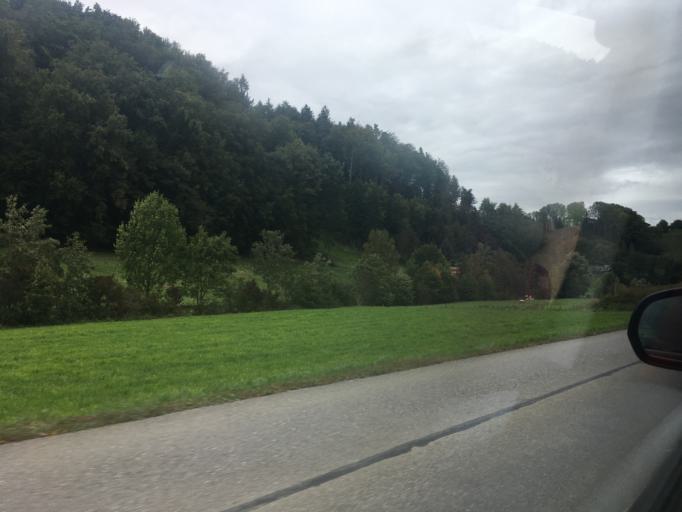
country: CH
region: Fribourg
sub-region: Sense District
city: Sankt Antoni
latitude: 46.8182
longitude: 7.2493
